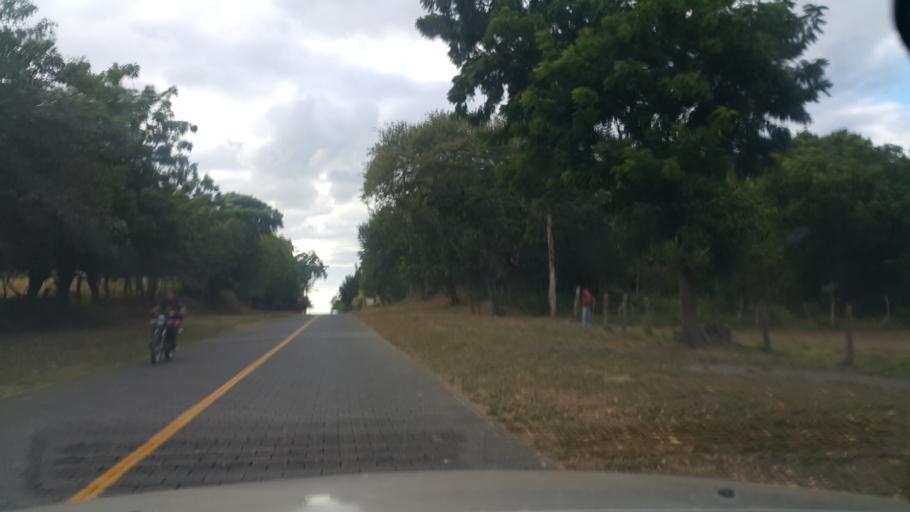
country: NI
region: Rivas
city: Moyogalpa
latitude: 11.4938
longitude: -85.6763
